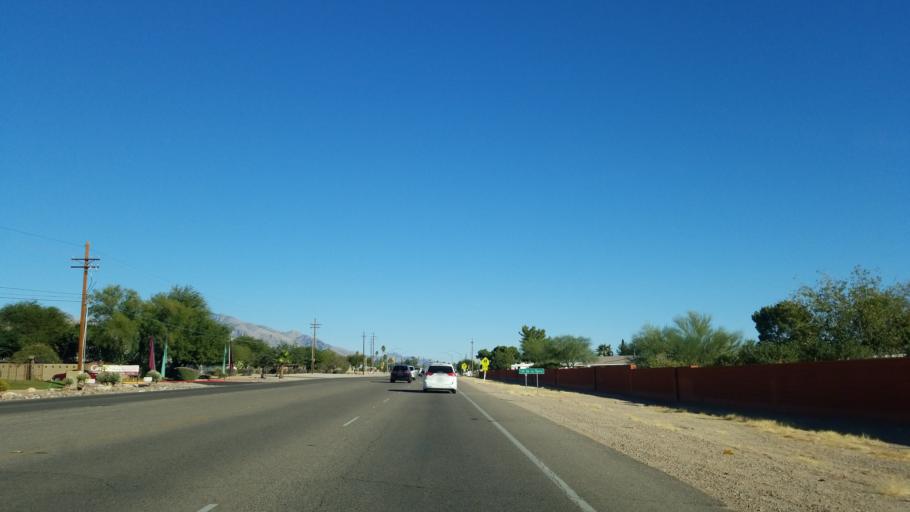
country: US
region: Arizona
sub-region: Pima County
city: Flowing Wells
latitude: 32.3232
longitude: -111.0411
